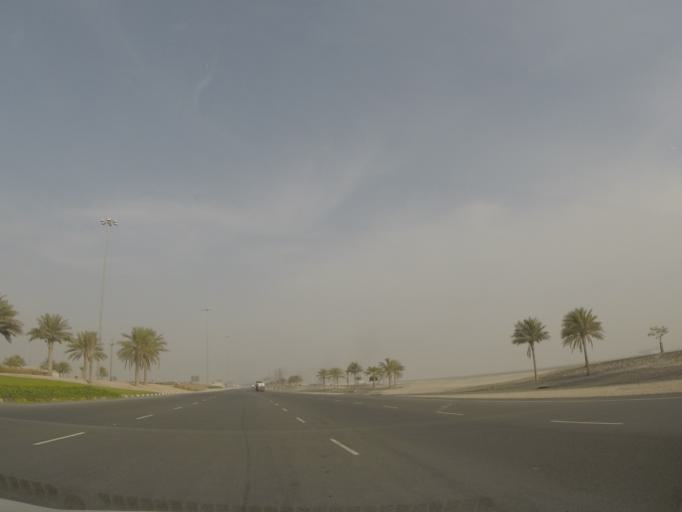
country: AE
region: Abu Dhabi
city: Abu Dhabi
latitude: 24.7811
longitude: 54.7042
